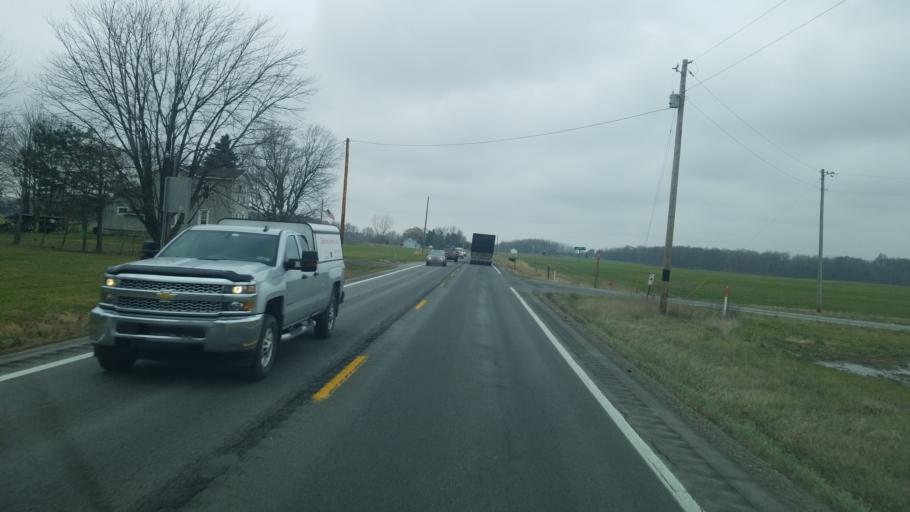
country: US
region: Ohio
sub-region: Huron County
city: Greenwich
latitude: 41.1067
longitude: -82.4988
